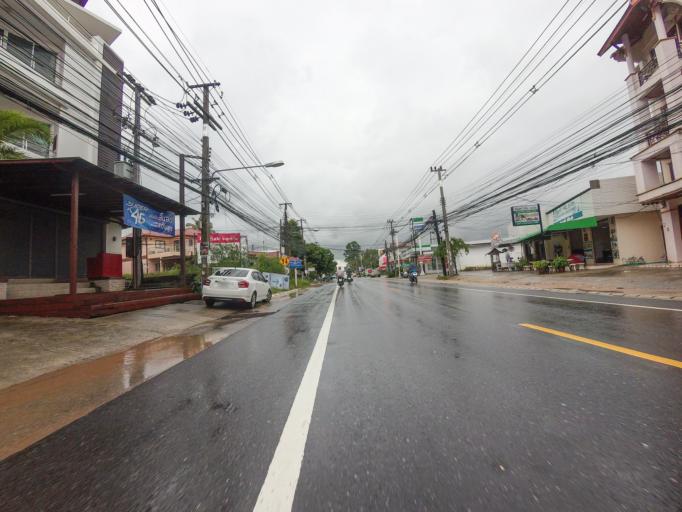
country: TH
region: Surat Thani
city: Ko Samui
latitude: 9.5134
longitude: 100.0508
